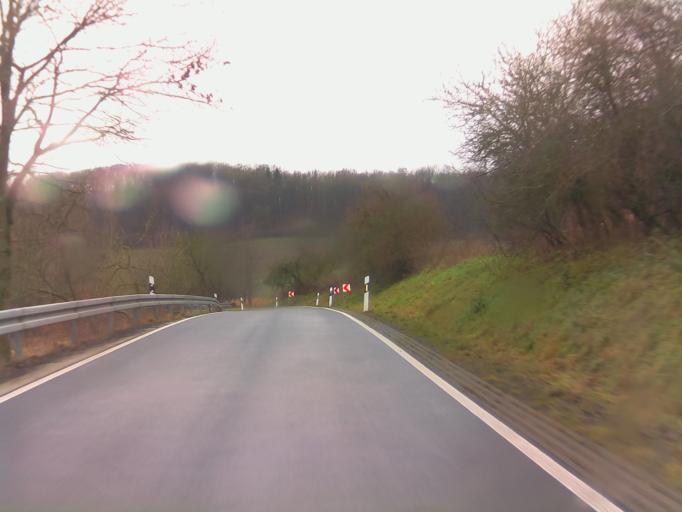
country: DE
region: Hesse
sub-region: Regierungsbezirk Kassel
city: Hofbieber
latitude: 50.5823
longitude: 9.8542
